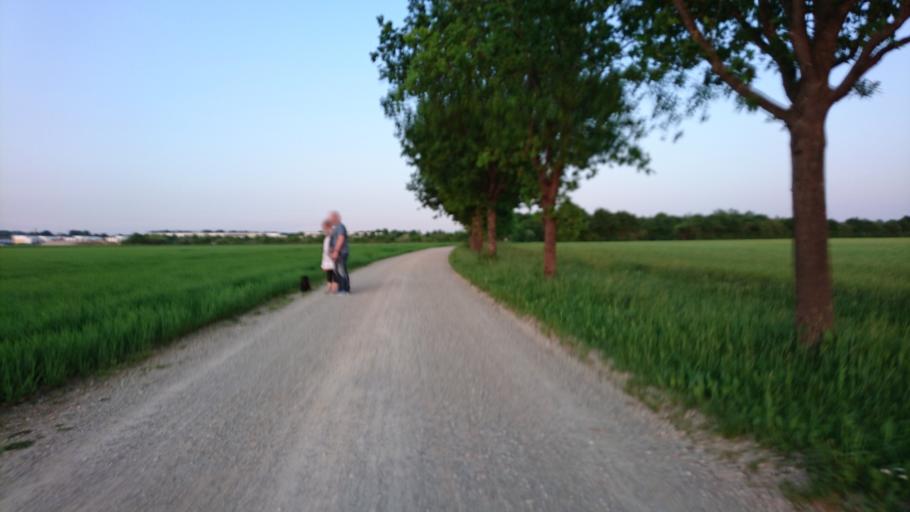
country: DE
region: Bavaria
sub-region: Upper Bavaria
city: Pliening
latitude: 48.1787
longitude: 11.7876
